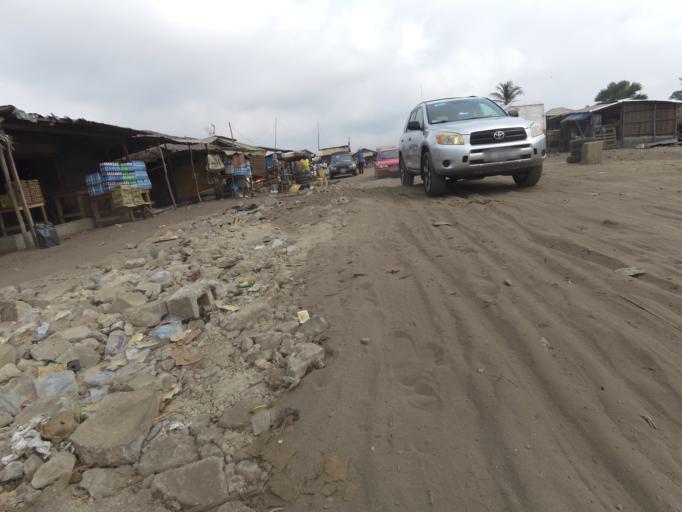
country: BJ
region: Queme
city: Porto-Novo
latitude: 6.3826
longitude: 2.7066
